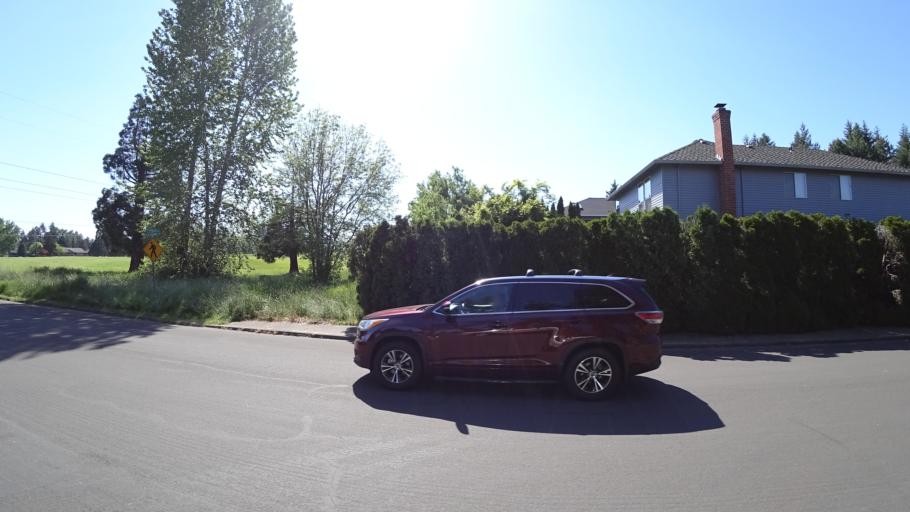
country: US
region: Oregon
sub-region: Washington County
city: Rockcreek
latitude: 45.5581
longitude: -122.8791
